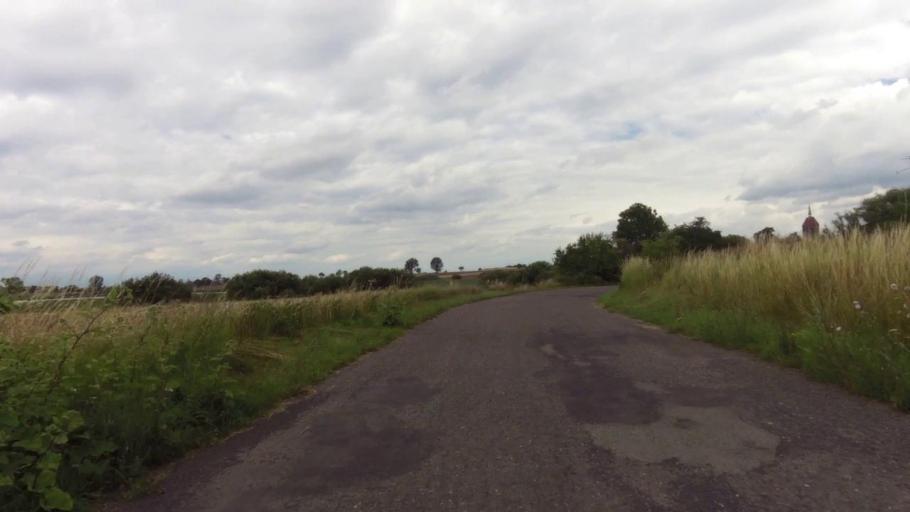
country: PL
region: West Pomeranian Voivodeship
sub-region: Powiat gryfinski
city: Moryn
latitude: 52.8689
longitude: 14.3296
